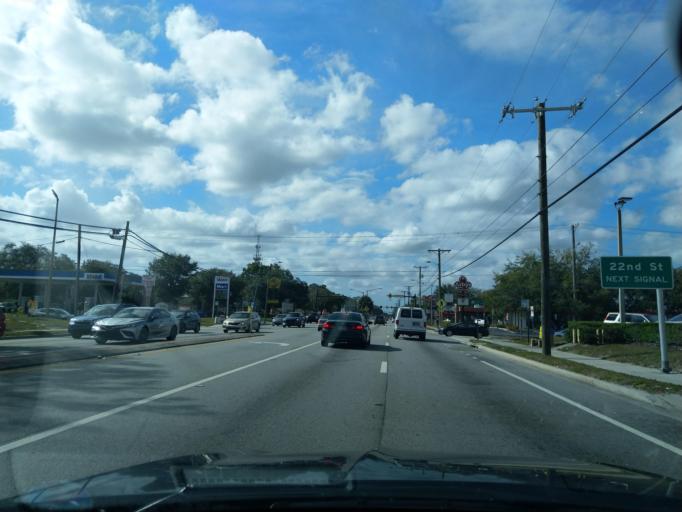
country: US
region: Florida
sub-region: Hillsborough County
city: University
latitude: 28.0693
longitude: -82.4319
